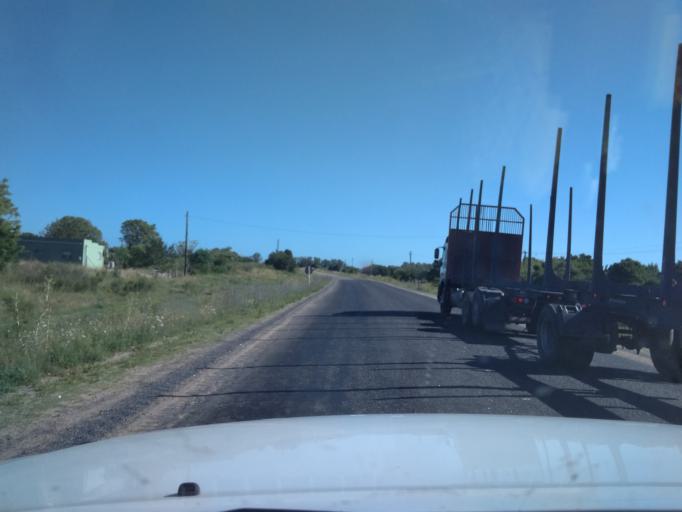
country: UY
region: Canelones
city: San Ramon
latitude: -34.2647
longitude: -55.9281
